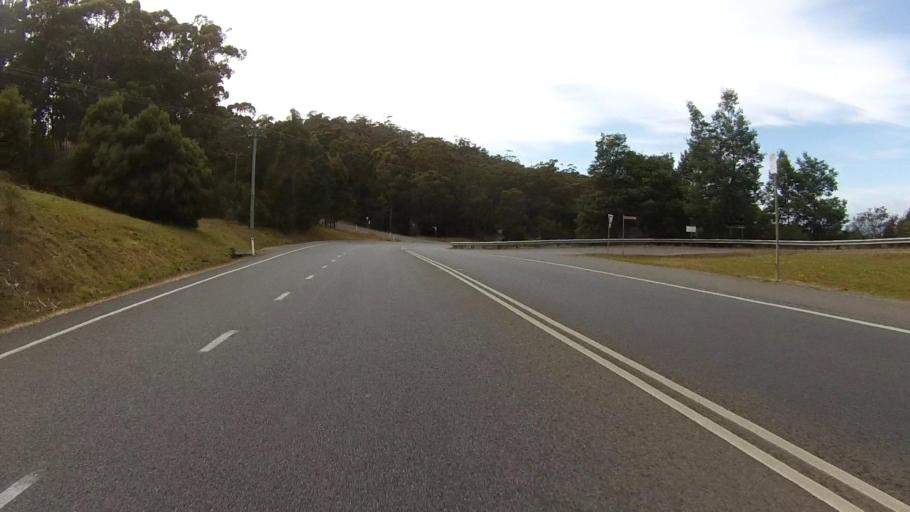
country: AU
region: Tasmania
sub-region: Kingborough
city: Kettering
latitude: -43.1126
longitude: 147.2431
